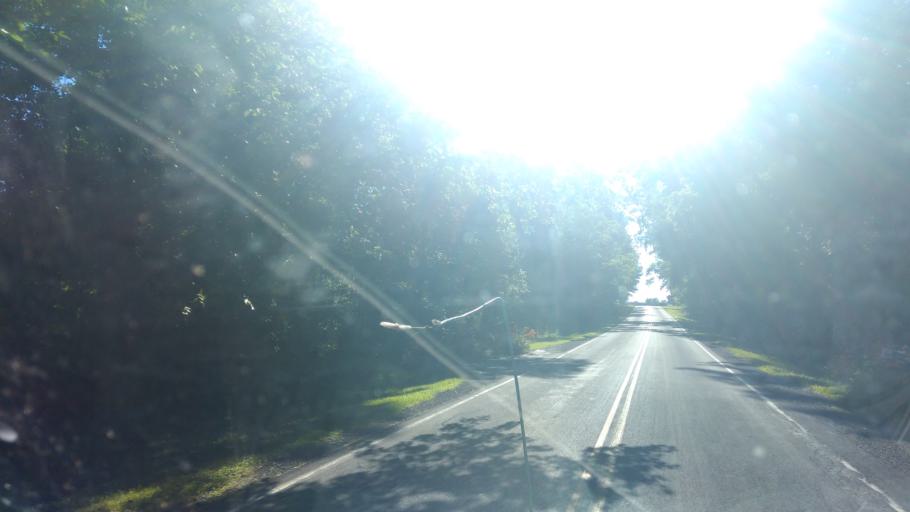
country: US
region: New York
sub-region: Wayne County
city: Lyons
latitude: 42.9990
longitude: -76.9522
